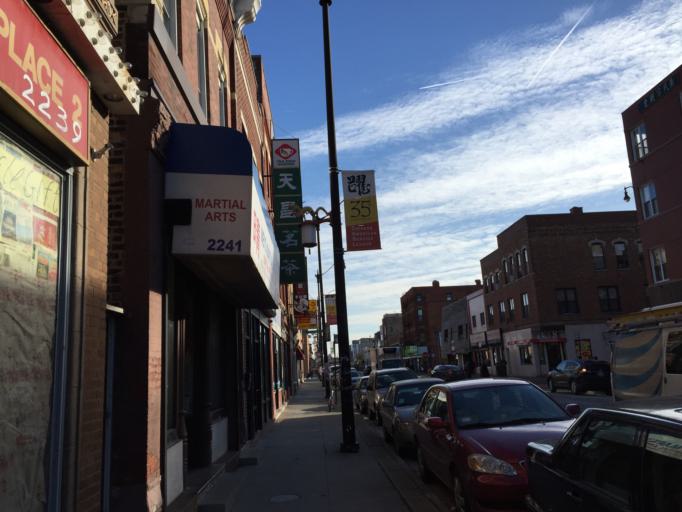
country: US
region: Illinois
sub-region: Cook County
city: Chicago
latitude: 41.8518
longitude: -87.6319
